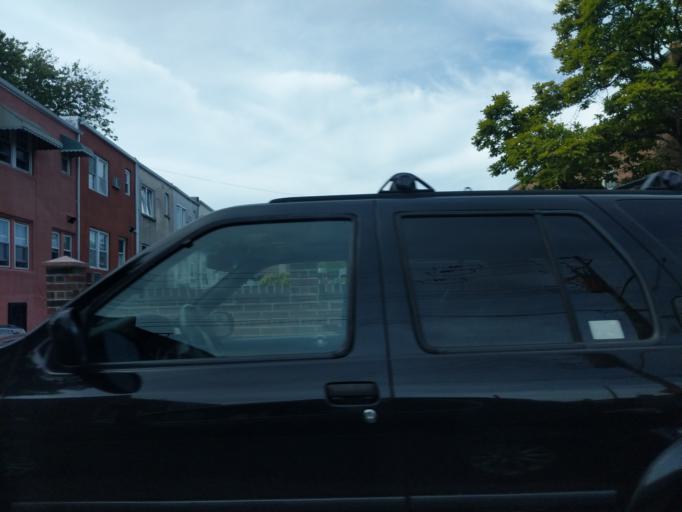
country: US
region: New York
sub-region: Kings County
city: East New York
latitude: 40.7162
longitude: -73.8847
